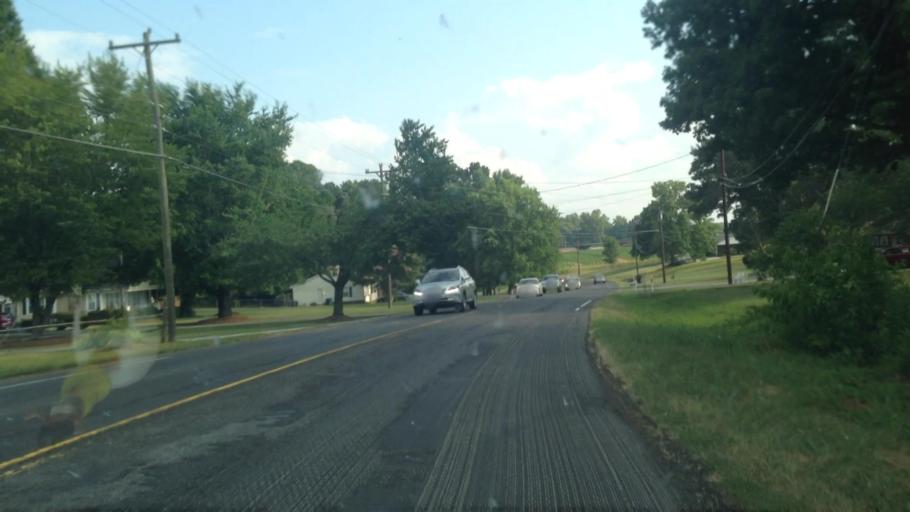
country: US
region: North Carolina
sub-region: Forsyth County
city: Kernersville
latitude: 36.0544
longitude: -80.0652
